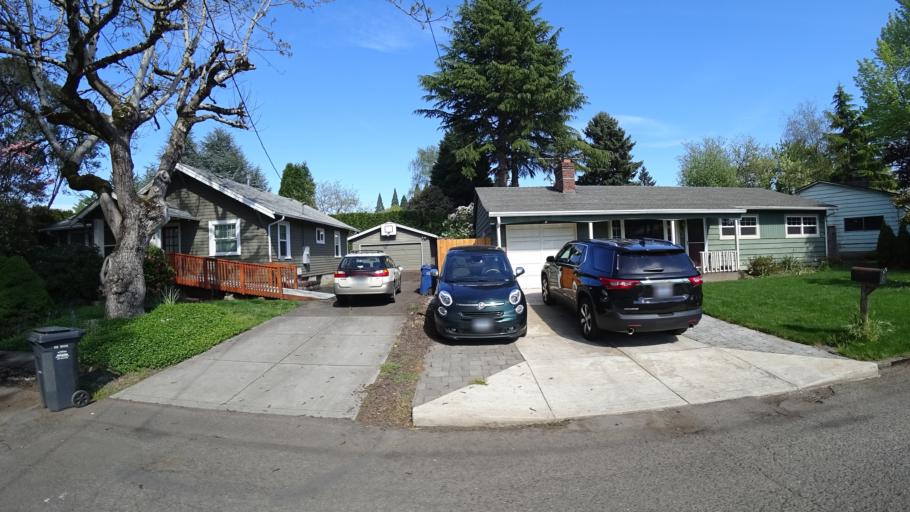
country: US
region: Oregon
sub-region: Clackamas County
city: Milwaukie
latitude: 45.4574
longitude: -122.6228
